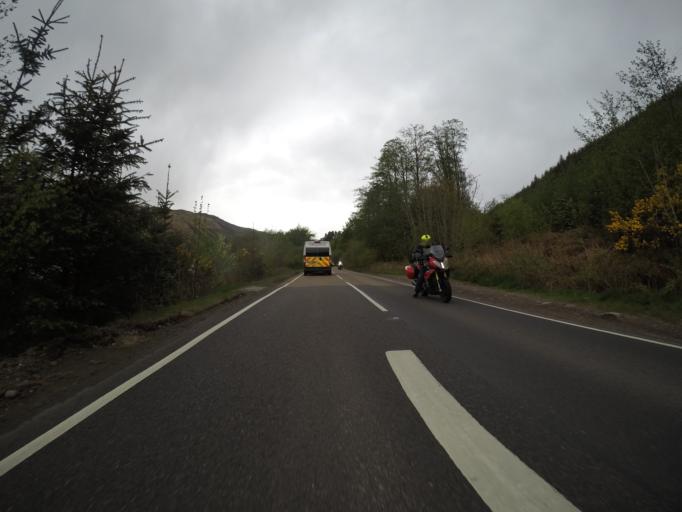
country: GB
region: Scotland
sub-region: Highland
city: Spean Bridge
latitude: 57.0222
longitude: -4.8241
